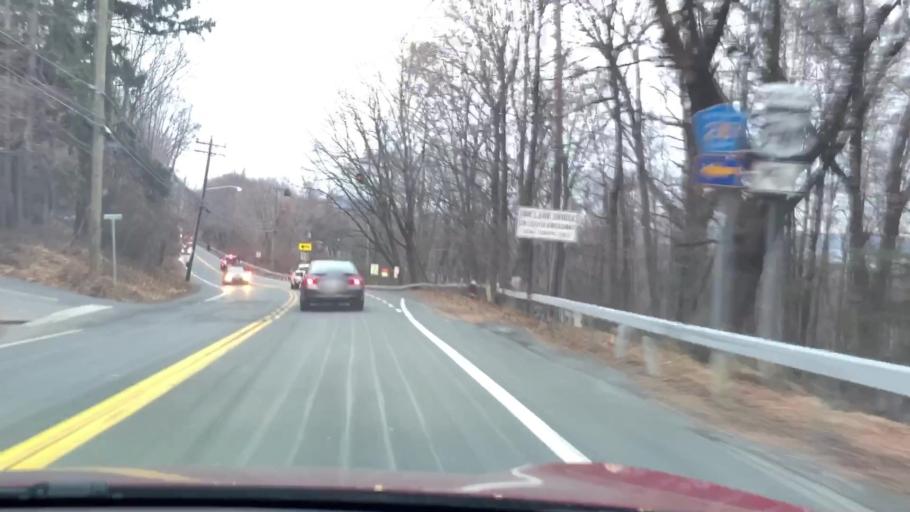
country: US
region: New York
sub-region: Rockland County
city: South Nyack
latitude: 41.0722
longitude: -73.9227
